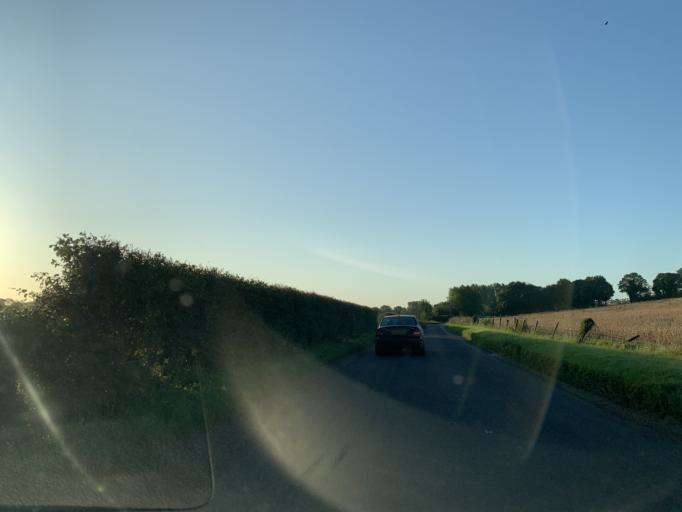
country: GB
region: England
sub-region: Wiltshire
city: Woodford
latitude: 51.1003
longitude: -1.8236
